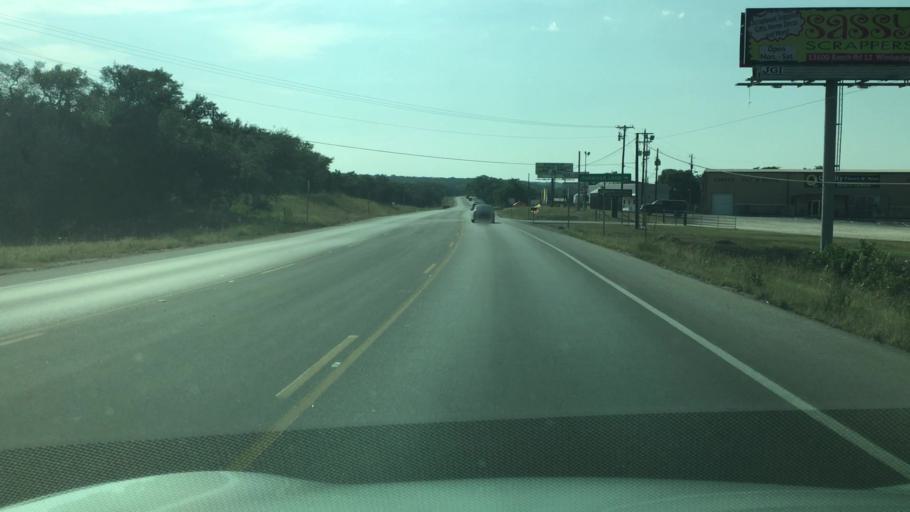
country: US
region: Texas
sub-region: Hays County
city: Wimberley
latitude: 29.9293
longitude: -98.0695
